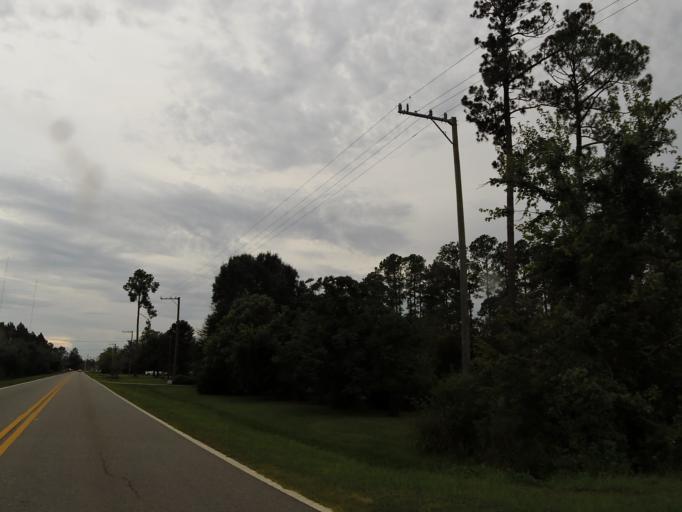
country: US
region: Florida
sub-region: Duval County
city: Baldwin
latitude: 30.3065
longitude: -82.0084
